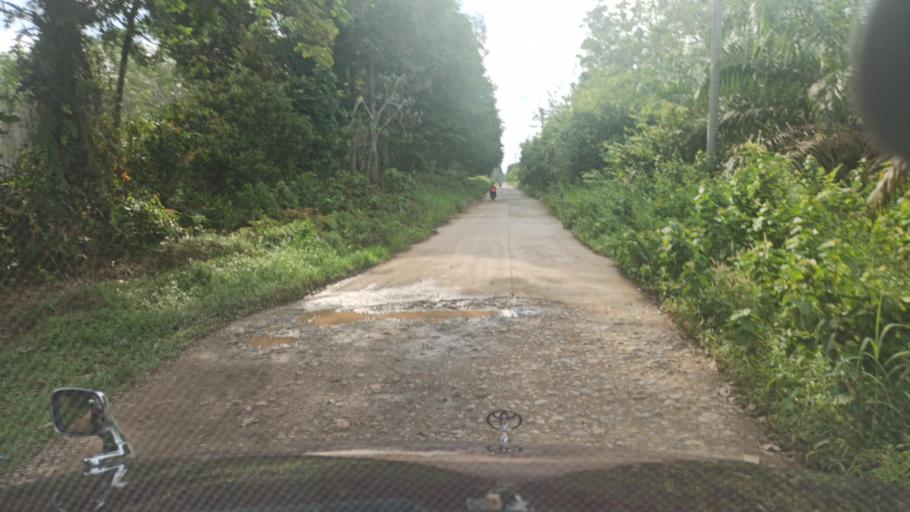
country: ID
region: South Sumatra
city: Gunungmenang
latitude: -3.2050
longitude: 103.9134
